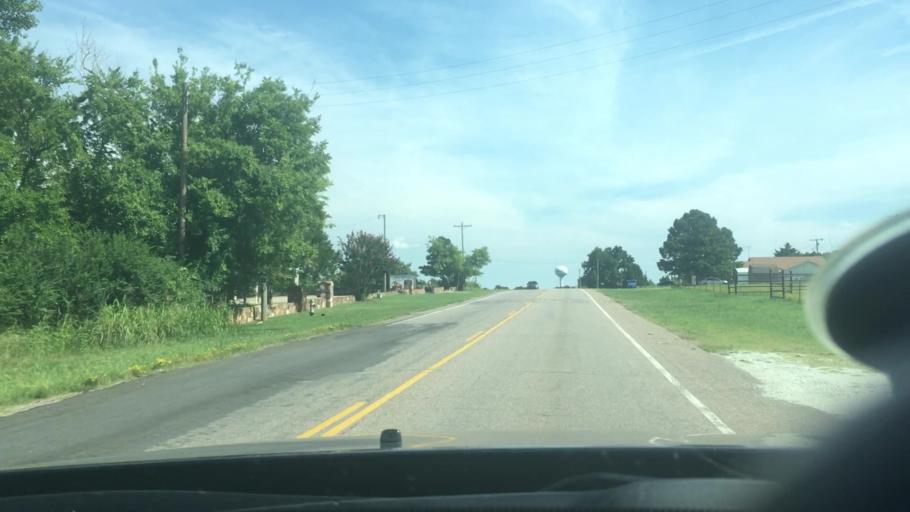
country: US
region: Oklahoma
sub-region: Seminole County
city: Seminole
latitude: 35.2430
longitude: -96.6981
